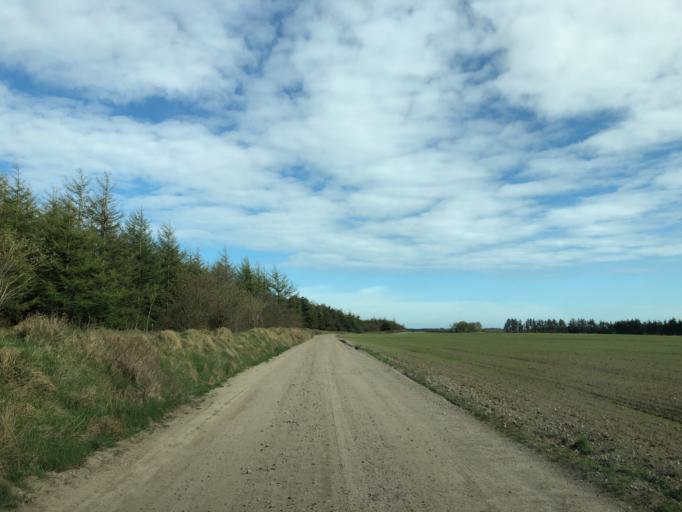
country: DK
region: Central Jutland
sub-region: Holstebro Kommune
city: Ulfborg
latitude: 56.2474
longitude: 8.3367
